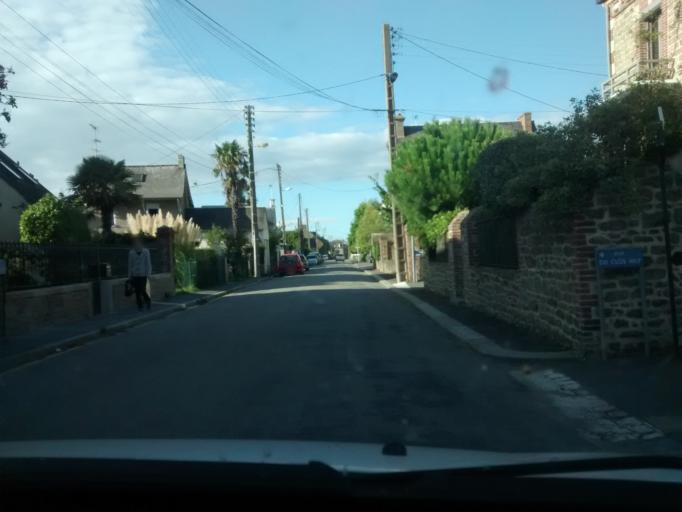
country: FR
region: Brittany
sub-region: Departement d'Ille-et-Vilaine
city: Dinard
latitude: 48.6310
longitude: -2.0675
